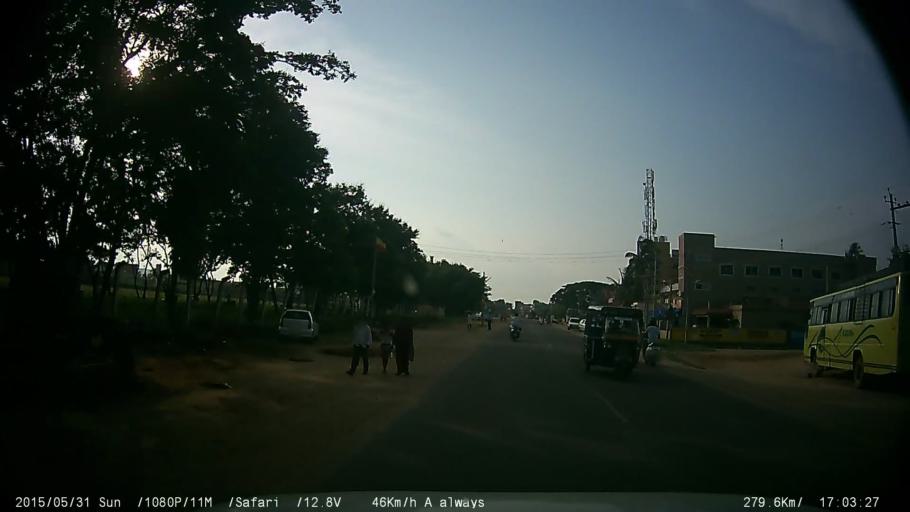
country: IN
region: Karnataka
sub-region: Chamrajnagar
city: Gundlupet
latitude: 11.8127
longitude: 76.6867
